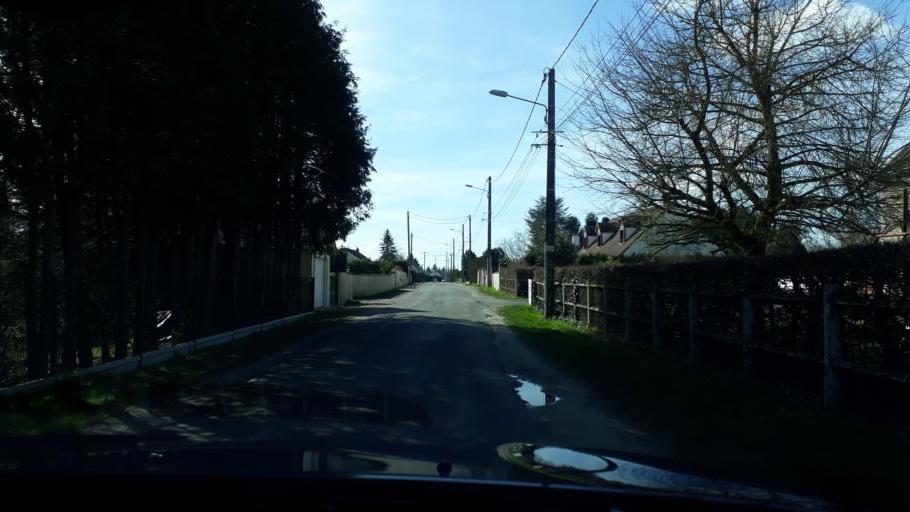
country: FR
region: Centre
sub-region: Departement du Loiret
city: Trainou
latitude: 47.9800
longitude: 2.1092
